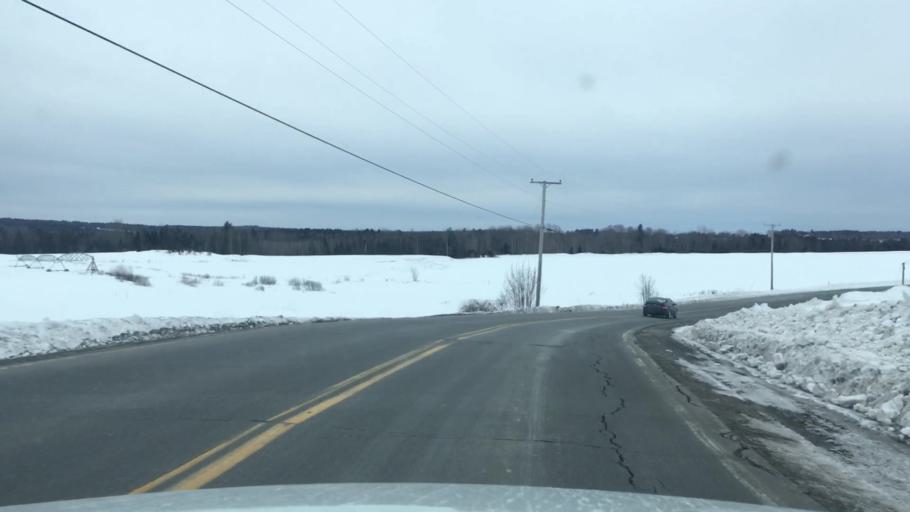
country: US
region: Maine
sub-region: Penobscot County
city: Garland
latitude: 44.9760
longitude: -69.0920
